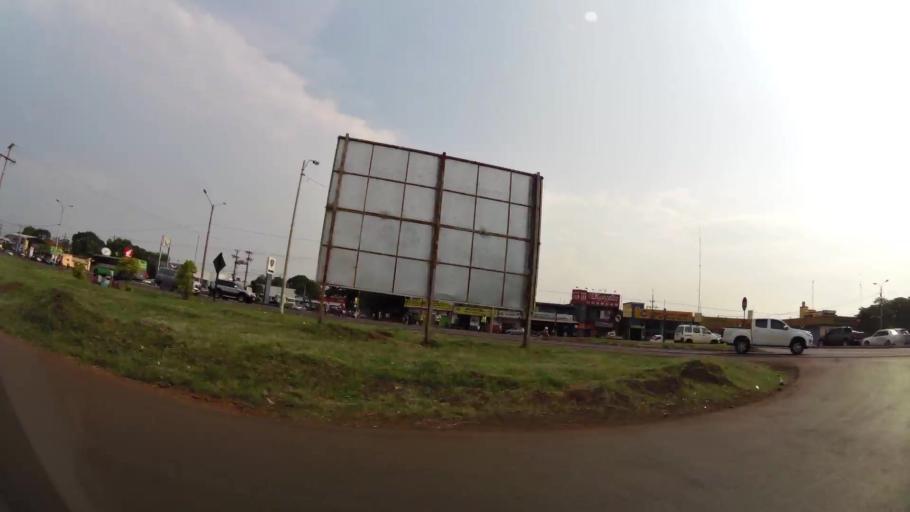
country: PY
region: Alto Parana
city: Ciudad del Este
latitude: -25.4985
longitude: -54.6631
